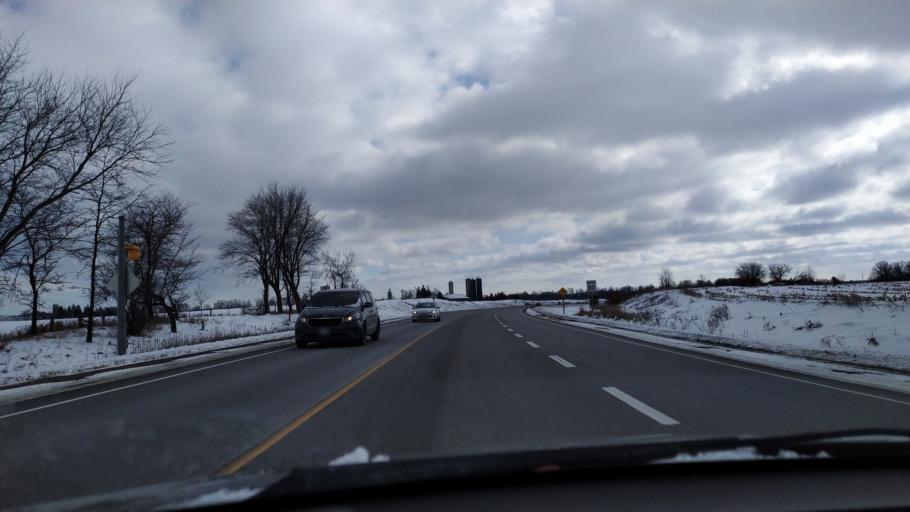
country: CA
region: Ontario
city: Waterloo
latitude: 43.5407
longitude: -80.5444
